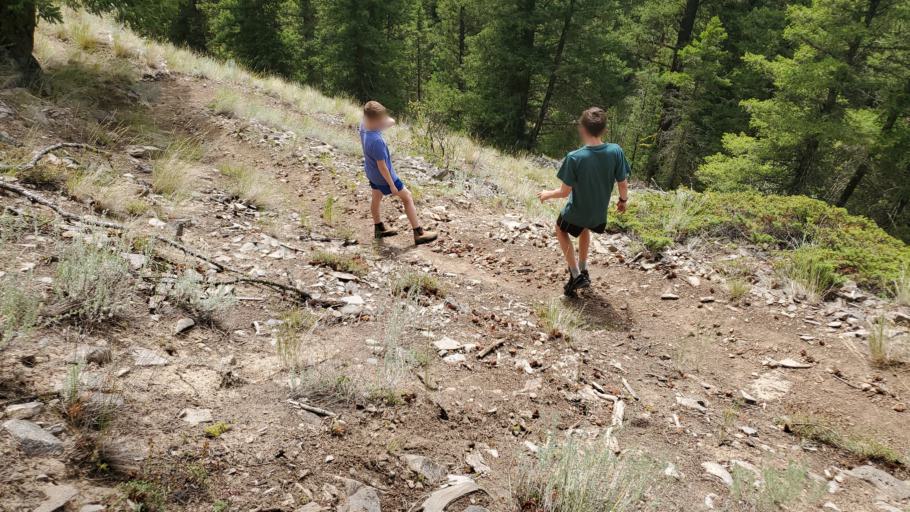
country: CA
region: British Columbia
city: Cache Creek
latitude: 51.4760
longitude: -121.3681
